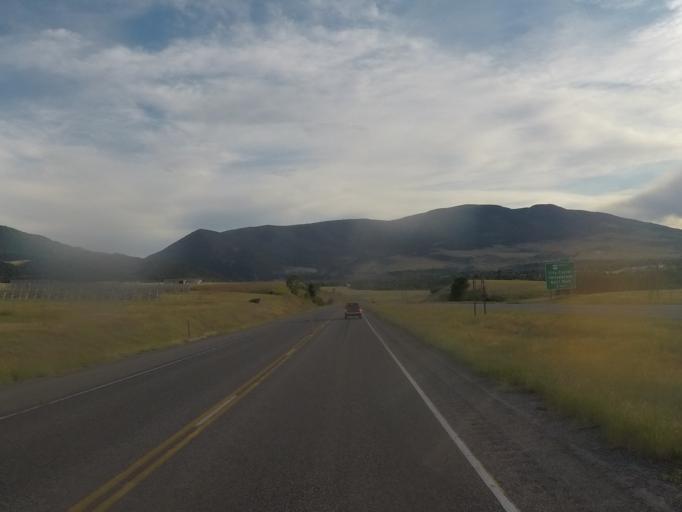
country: US
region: Montana
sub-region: Park County
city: Livingston
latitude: 45.6484
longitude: -110.5472
